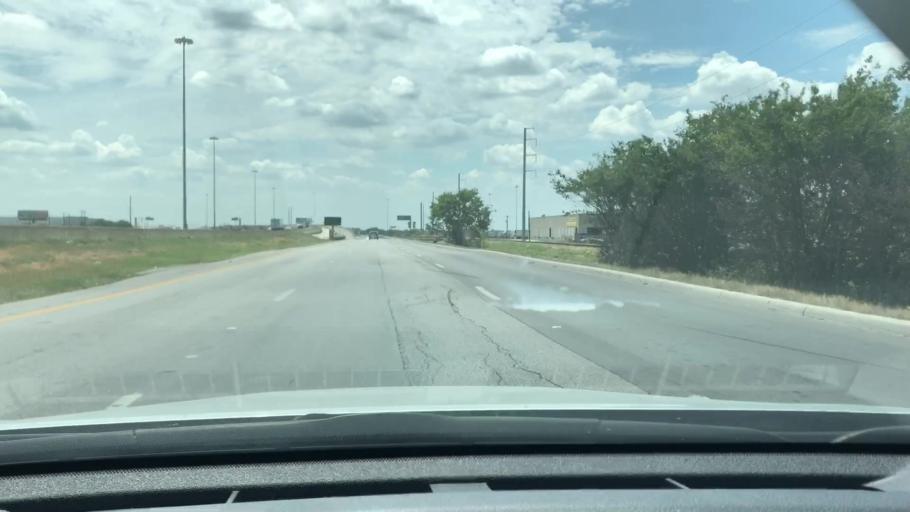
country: US
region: Texas
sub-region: Bexar County
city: Kirby
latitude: 29.4794
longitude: -98.4046
